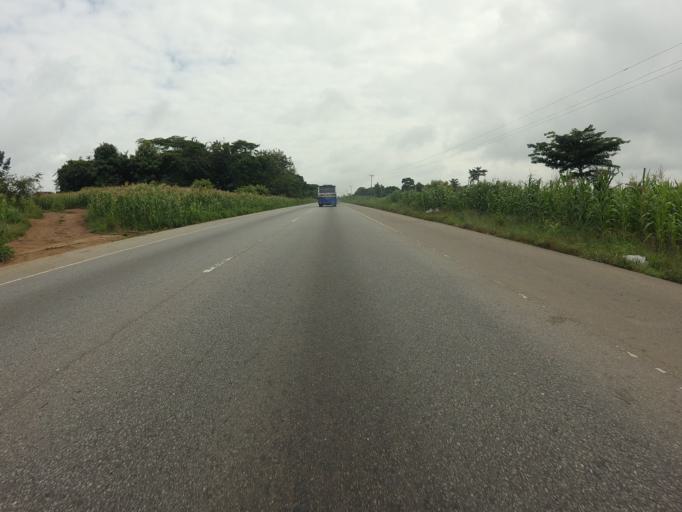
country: GH
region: Ashanti
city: Tafo
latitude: 6.9754
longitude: -1.6860
